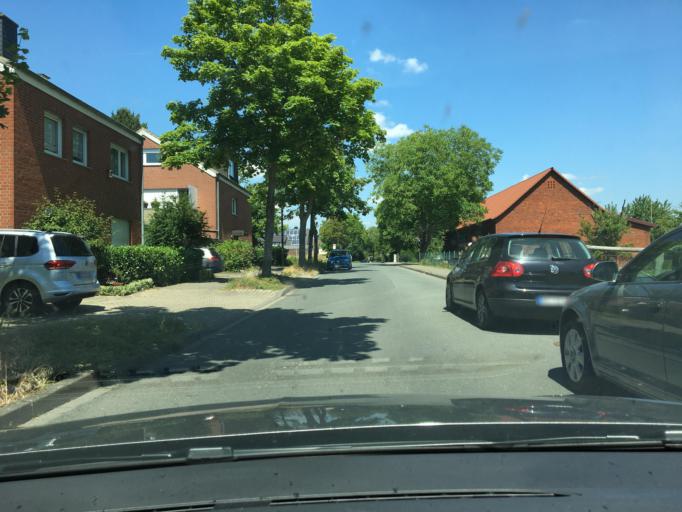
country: DE
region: North Rhine-Westphalia
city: Ahlen
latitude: 51.7736
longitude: 7.9037
